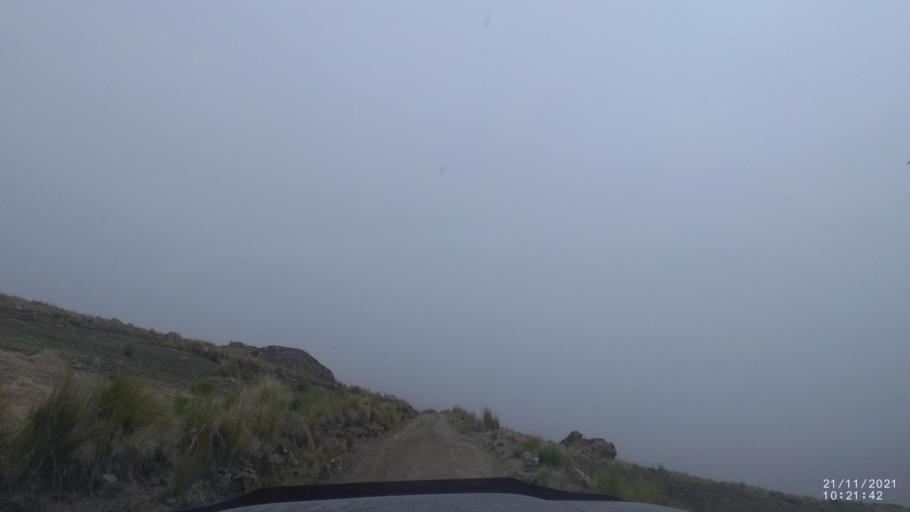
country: BO
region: Cochabamba
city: Cochabamba
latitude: -16.9871
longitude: -66.2593
